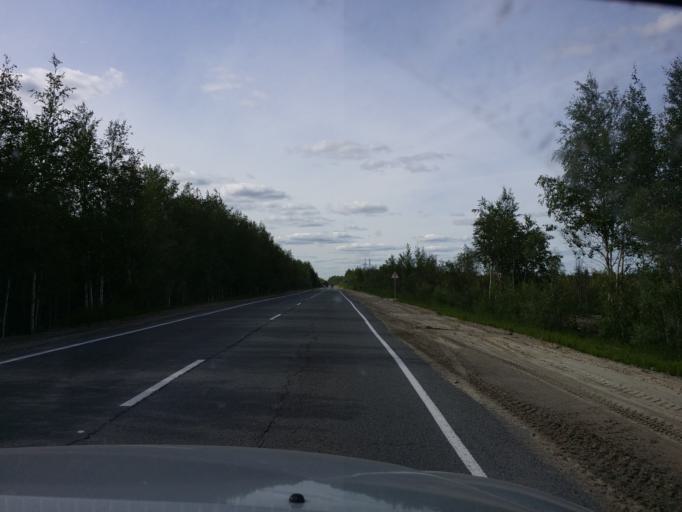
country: RU
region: Khanty-Mansiyskiy Avtonomnyy Okrug
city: Nizhnevartovsk
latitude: 61.1109
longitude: 76.6081
